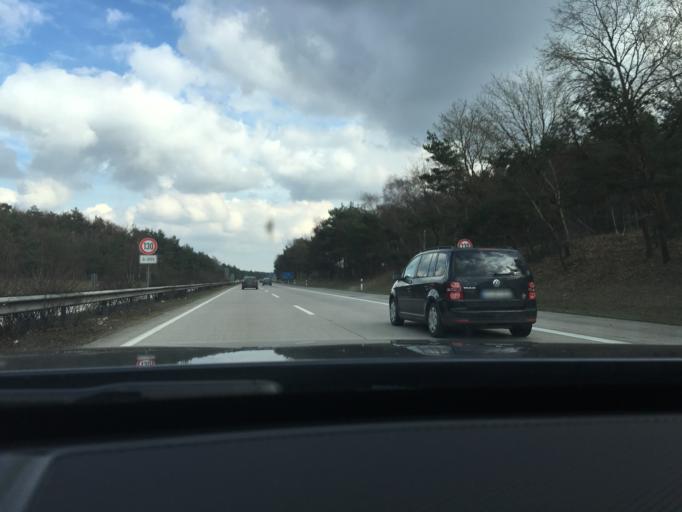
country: DE
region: Lower Saxony
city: Dotlingen
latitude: 52.9011
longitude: 8.3403
